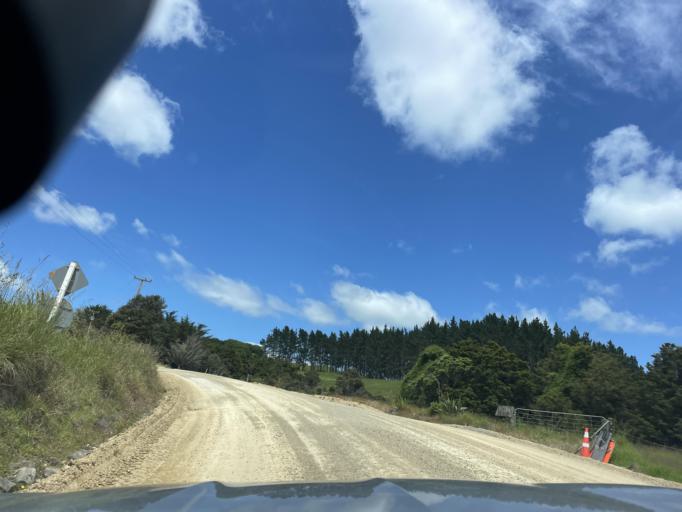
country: NZ
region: Auckland
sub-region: Auckland
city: Wellsford
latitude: -36.1458
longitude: 174.2824
